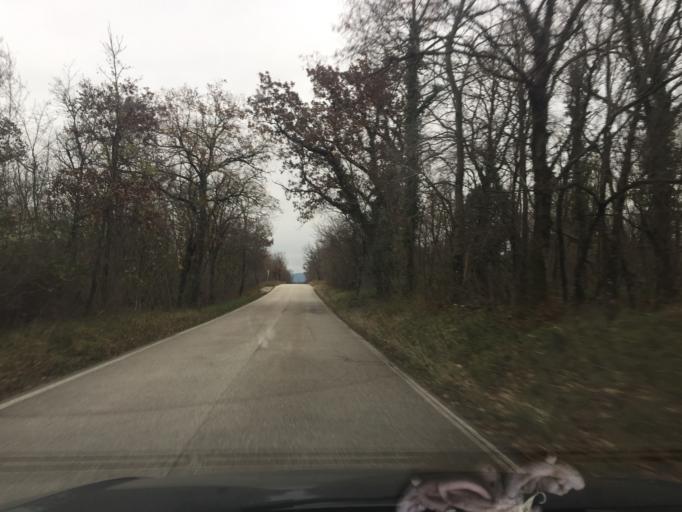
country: IT
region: Friuli Venezia Giulia
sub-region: Provincia di Trieste
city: Zolla
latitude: 45.7079
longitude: 13.8177
